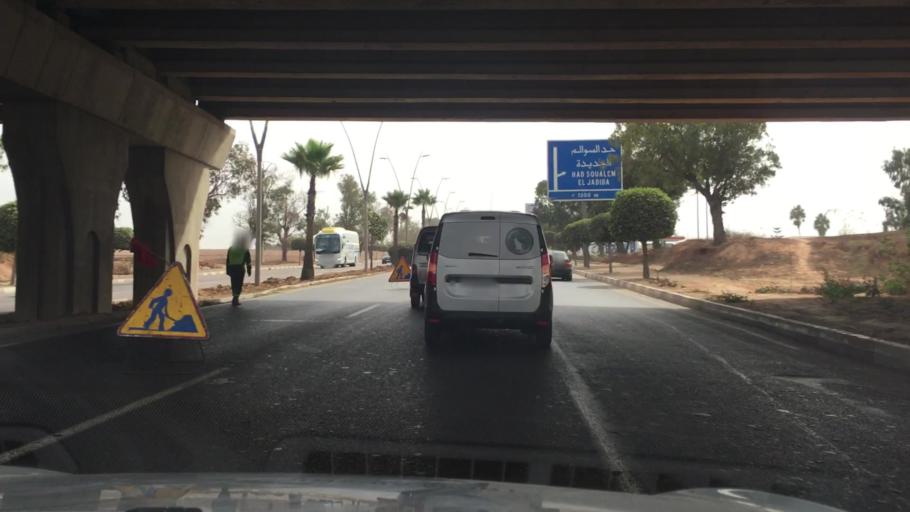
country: MA
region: Grand Casablanca
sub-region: Nouaceur
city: Bouskoura
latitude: 33.5118
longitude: -7.6308
